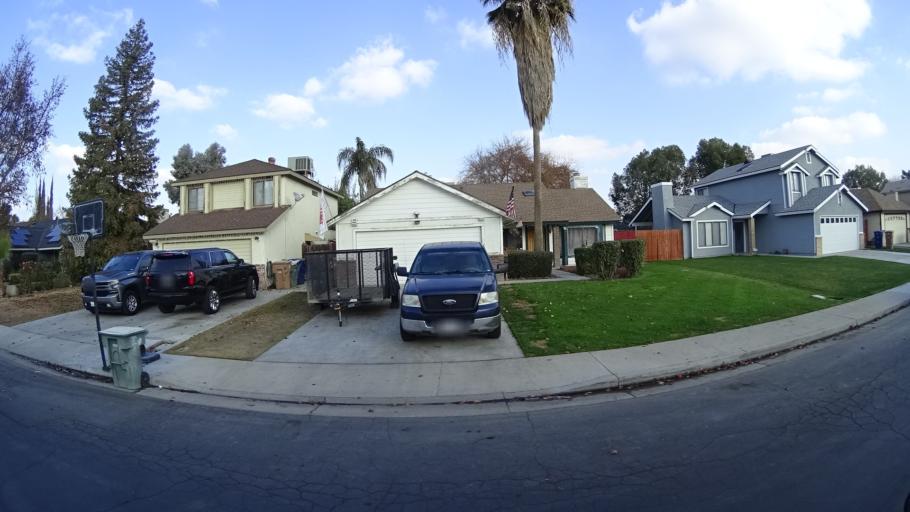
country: US
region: California
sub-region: Kern County
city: Greenacres
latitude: 35.3126
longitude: -119.1044
